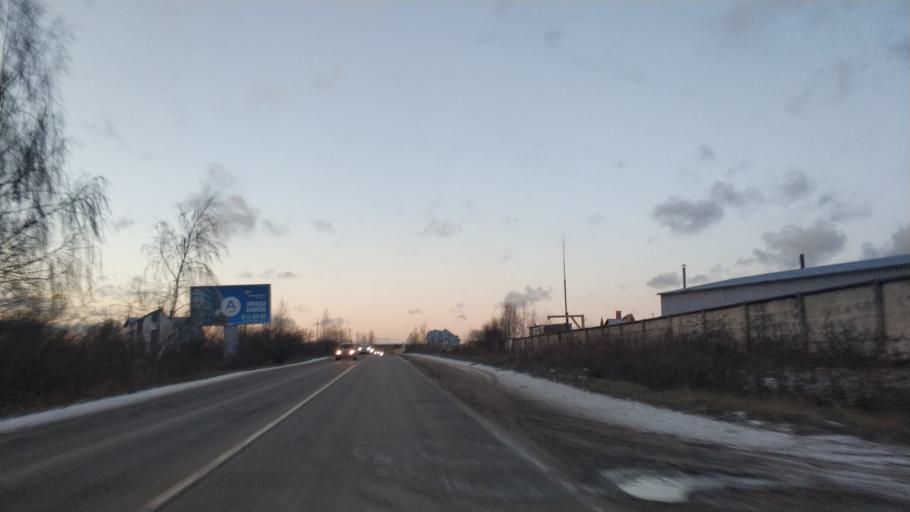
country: RU
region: St.-Petersburg
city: Pontonnyy
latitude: 59.8102
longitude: 30.6119
